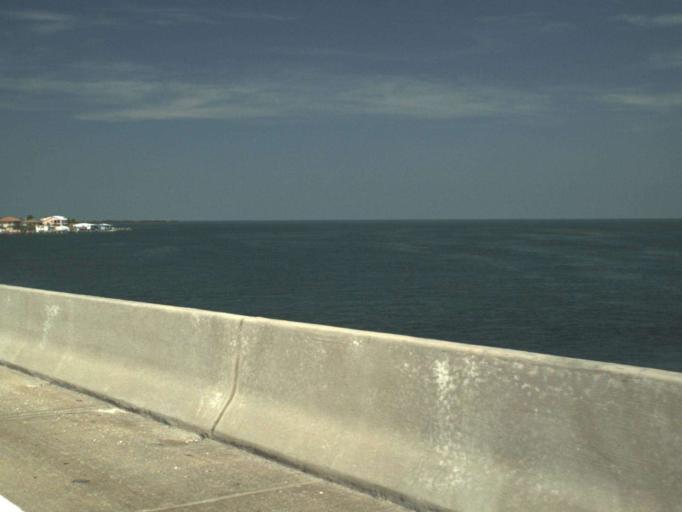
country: US
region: Florida
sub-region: Monroe County
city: Marathon
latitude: 24.7915
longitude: -80.8834
